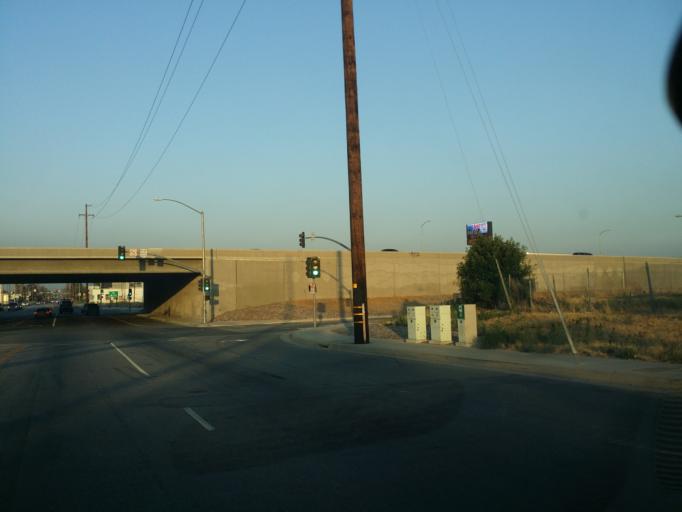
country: US
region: California
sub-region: San Bernardino County
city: San Bernardino
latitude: 34.0921
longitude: -117.3029
